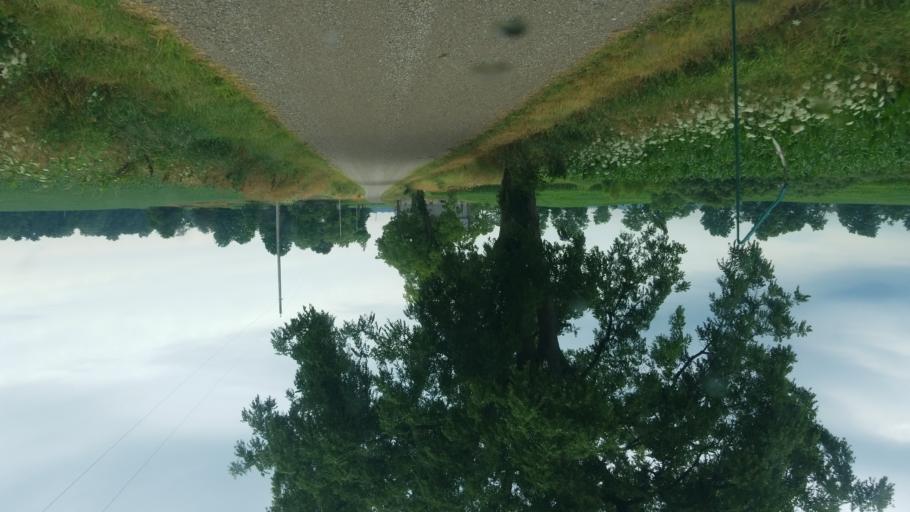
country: US
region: Indiana
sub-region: Steuben County
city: Hamilton
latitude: 41.5027
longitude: -84.9407
